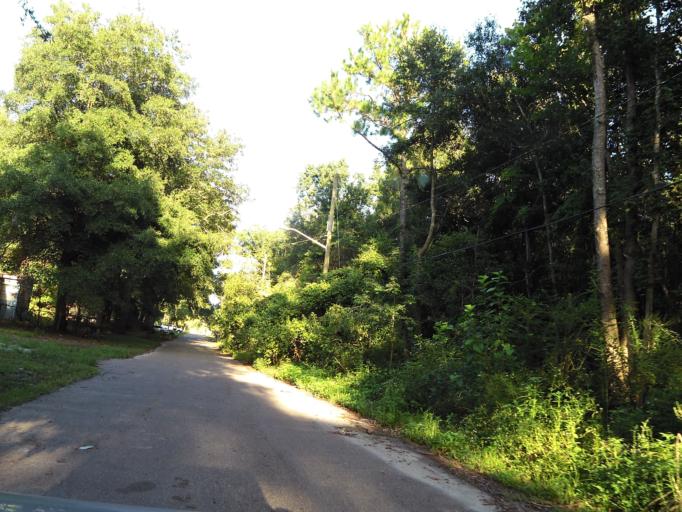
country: US
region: Florida
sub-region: Duval County
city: Jacksonville
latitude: 30.3435
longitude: -81.6964
